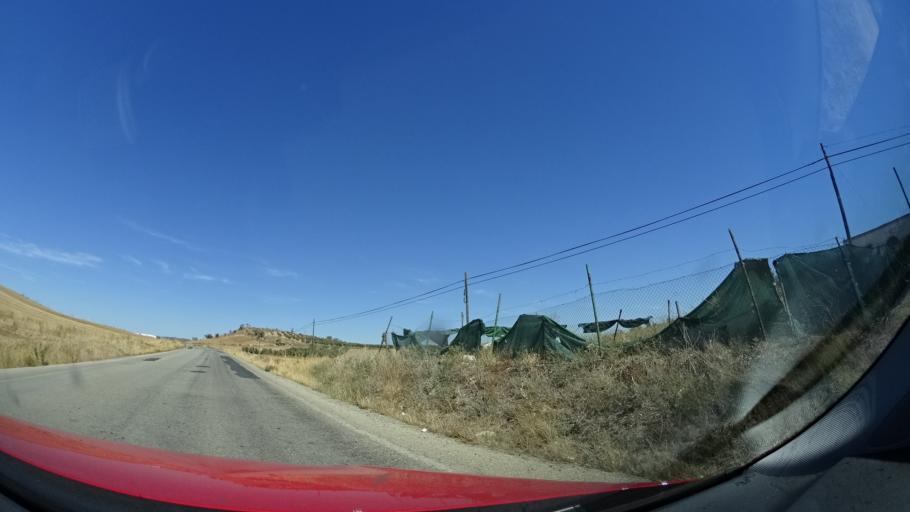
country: ES
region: Andalusia
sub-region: Provincia de Malaga
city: Campillos
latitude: 37.0605
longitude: -4.8636
